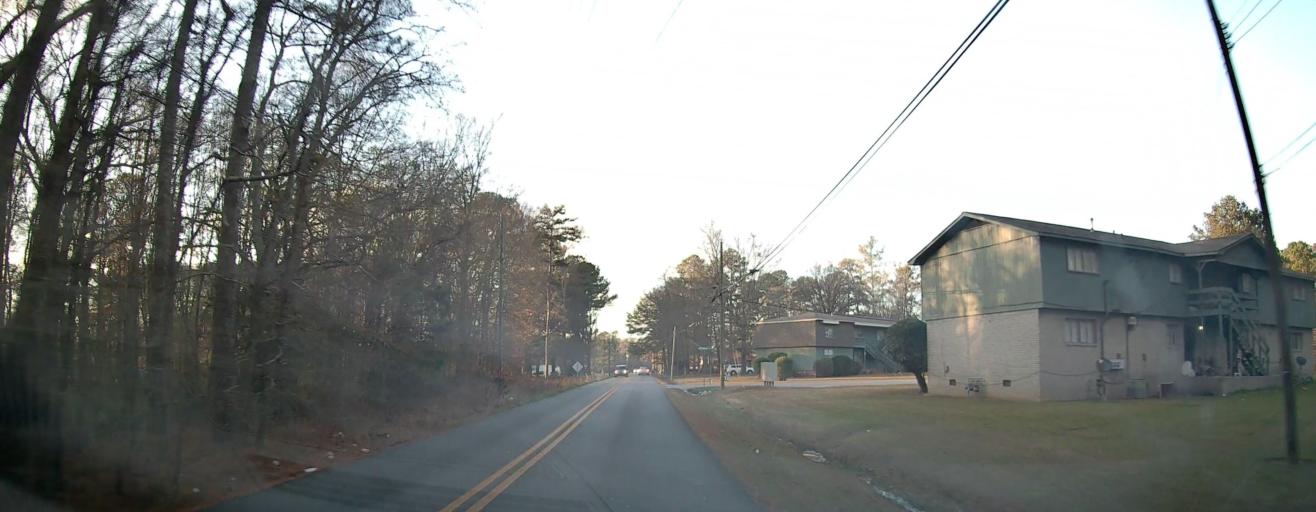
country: US
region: Alabama
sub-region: Etowah County
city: Glencoe
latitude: 33.9730
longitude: -85.9742
